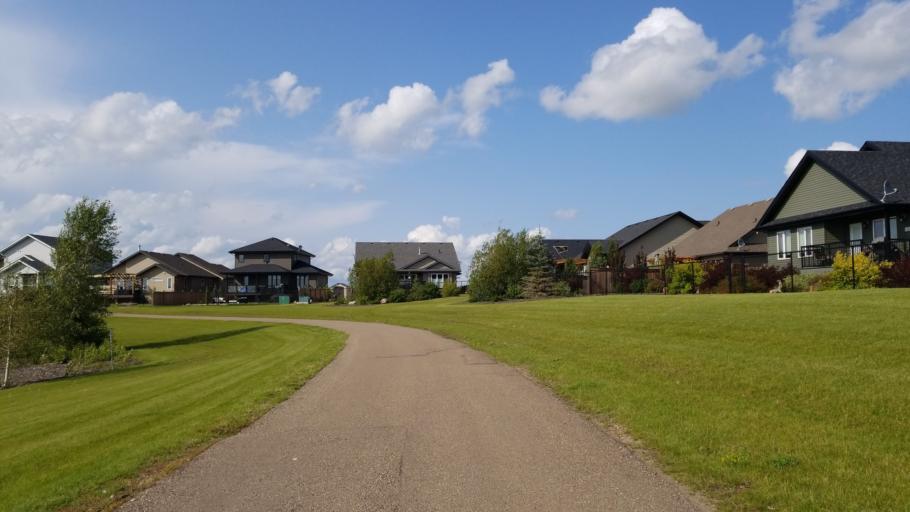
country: CA
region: Saskatchewan
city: Lloydminster
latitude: 53.2636
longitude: -110.0460
